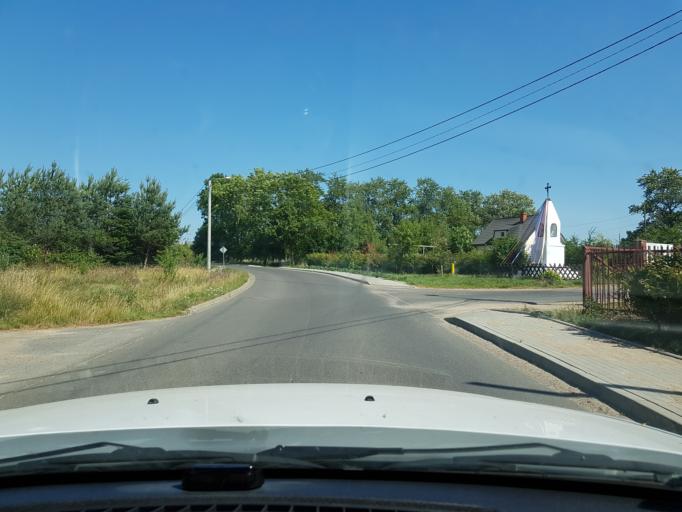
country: PL
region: West Pomeranian Voivodeship
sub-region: Powiat koszalinski
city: Mielno
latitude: 54.1867
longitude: 16.0730
